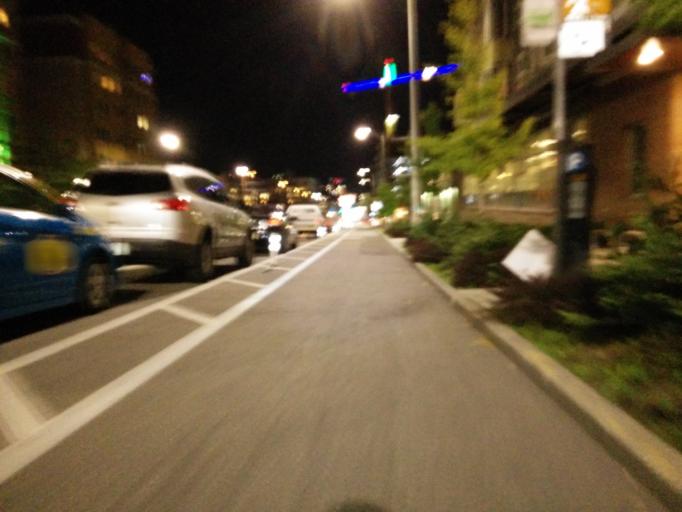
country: US
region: Washington
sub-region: King County
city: Seattle
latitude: 47.6200
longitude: -122.3422
